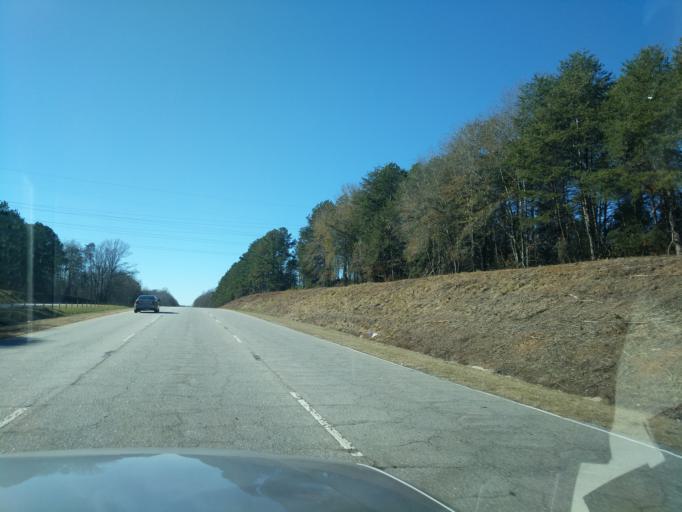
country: US
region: South Carolina
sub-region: Pickens County
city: Central
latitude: 34.7059
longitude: -82.7584
